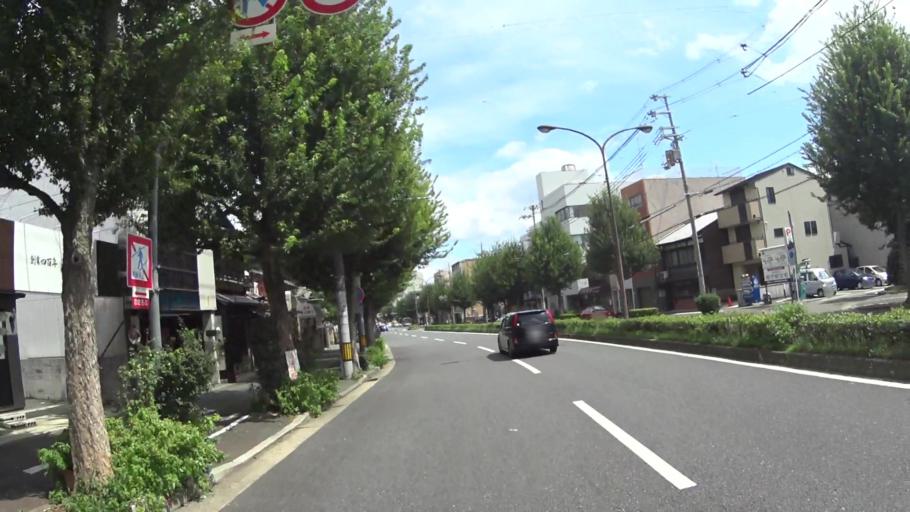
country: JP
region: Kyoto
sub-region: Kyoto-shi
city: Kamigyo-ku
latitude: 35.0408
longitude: 135.7451
